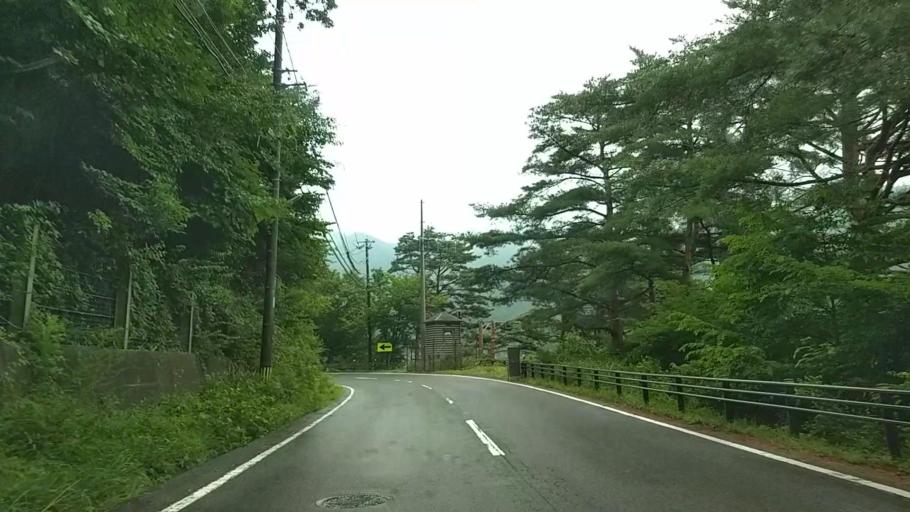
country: JP
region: Yamanashi
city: Fujikawaguchiko
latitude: 35.4872
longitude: 138.6044
